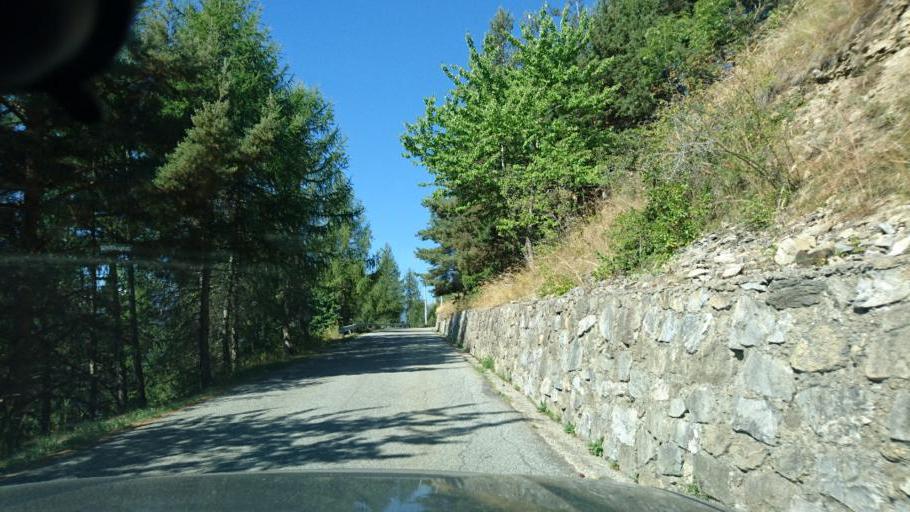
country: IT
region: Aosta Valley
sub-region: Valle d'Aosta
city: Saint-Nicolas
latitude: 45.7193
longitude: 7.1574
